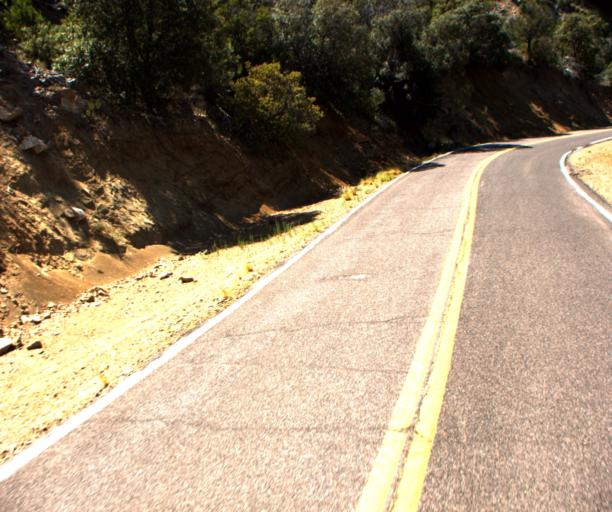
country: US
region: Arizona
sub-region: Graham County
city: Swift Trail Junction
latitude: 32.6547
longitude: -109.8052
